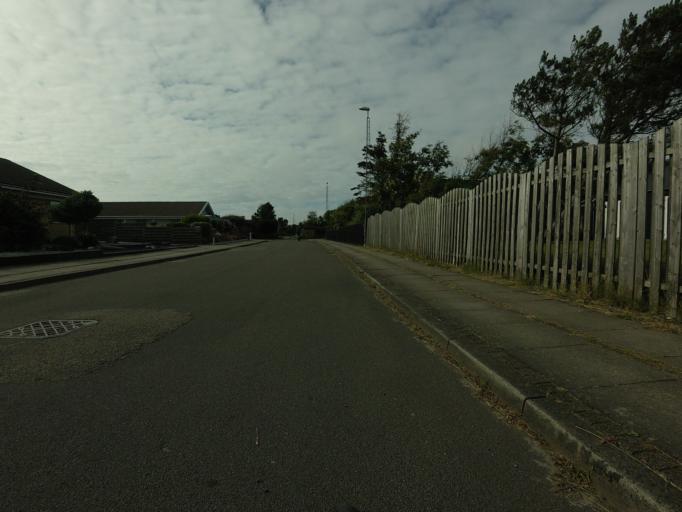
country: DK
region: North Denmark
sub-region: Jammerbugt Kommune
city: Pandrup
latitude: 57.3713
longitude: 9.7245
